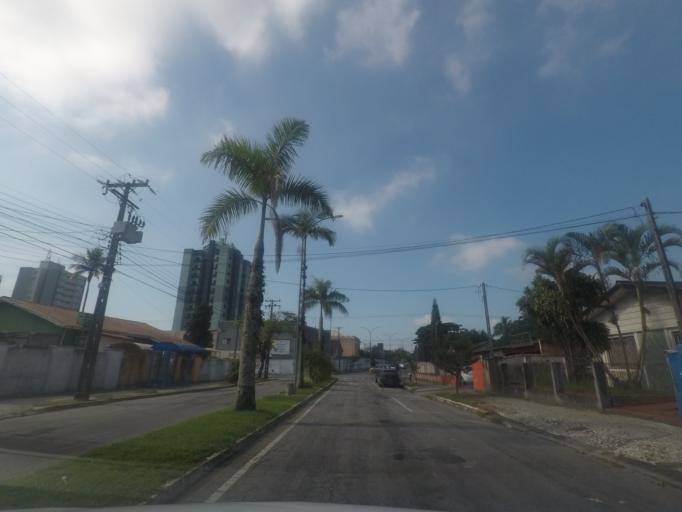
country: BR
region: Parana
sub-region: Paranagua
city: Paranagua
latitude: -25.5210
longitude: -48.5129
